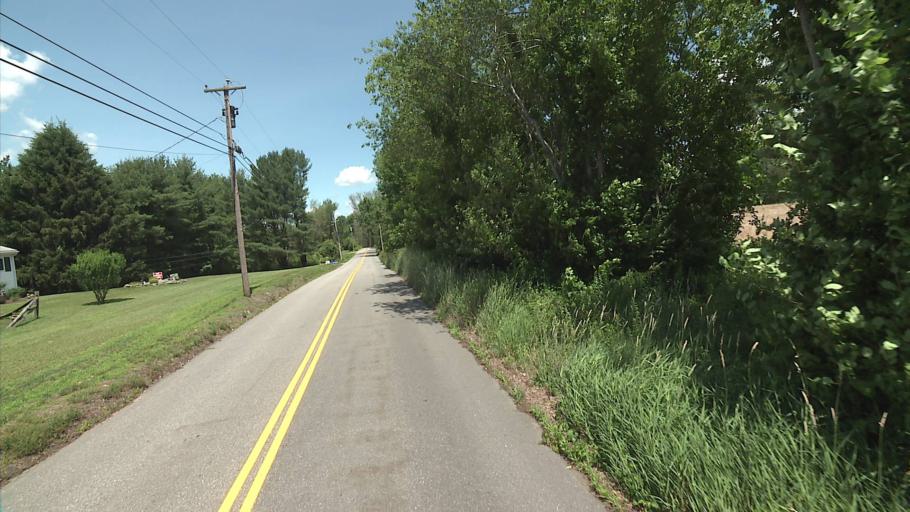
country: US
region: Connecticut
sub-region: New London County
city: Jewett City
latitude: 41.6044
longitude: -71.9106
